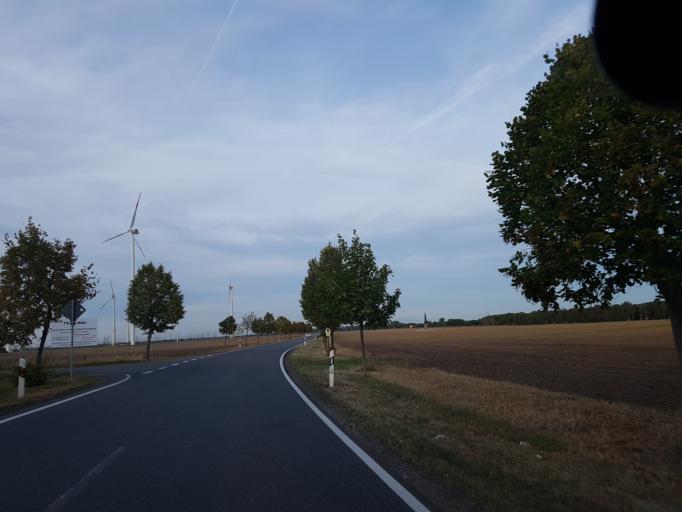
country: DE
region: Saxony
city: Glaubitz
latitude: 51.3329
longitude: 13.3754
